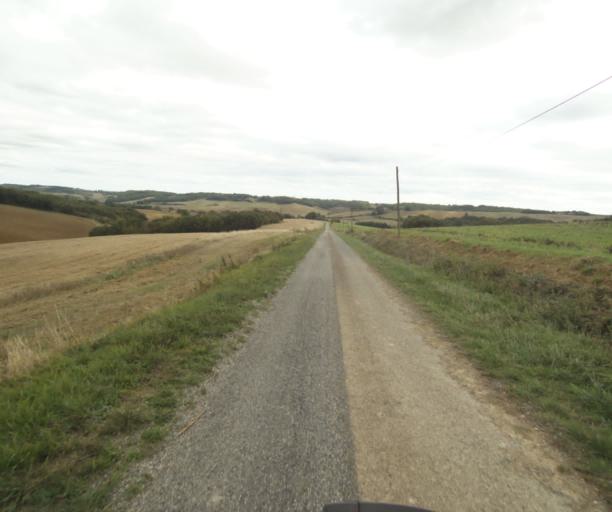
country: FR
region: Midi-Pyrenees
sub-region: Departement du Tarn-et-Garonne
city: Beaumont-de-Lomagne
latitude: 43.8545
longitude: 1.0713
